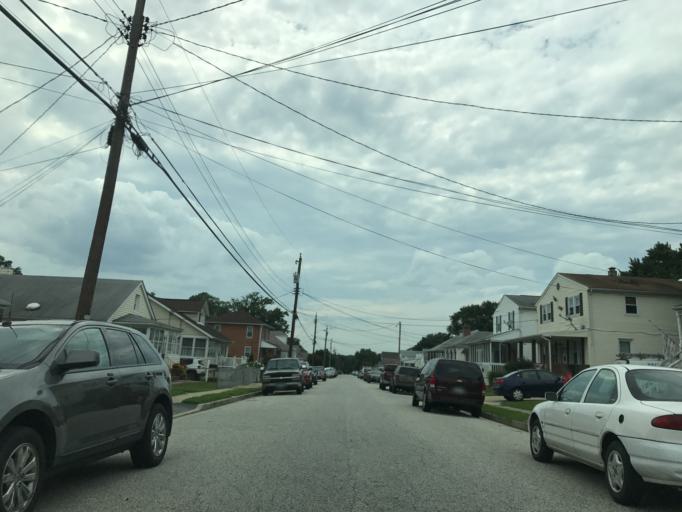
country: US
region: Maryland
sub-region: Baltimore County
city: Essex
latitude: 39.3129
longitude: -76.4794
